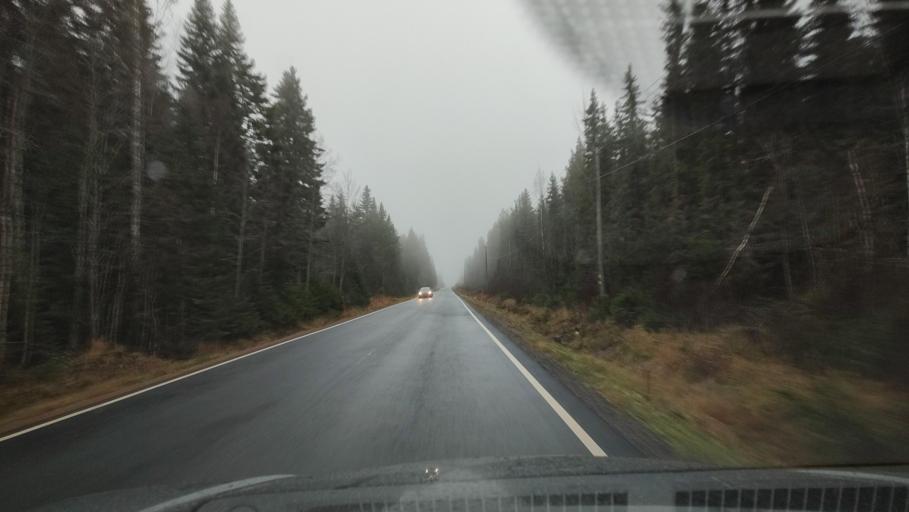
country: FI
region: Southern Ostrobothnia
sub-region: Suupohja
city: Karijoki
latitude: 62.1803
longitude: 21.7742
